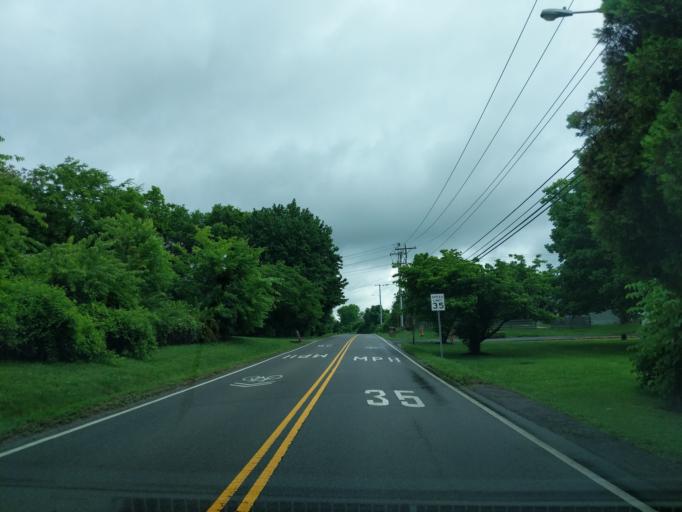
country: US
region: Tennessee
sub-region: Davidson County
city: Lakewood
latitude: 36.2253
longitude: -86.6884
